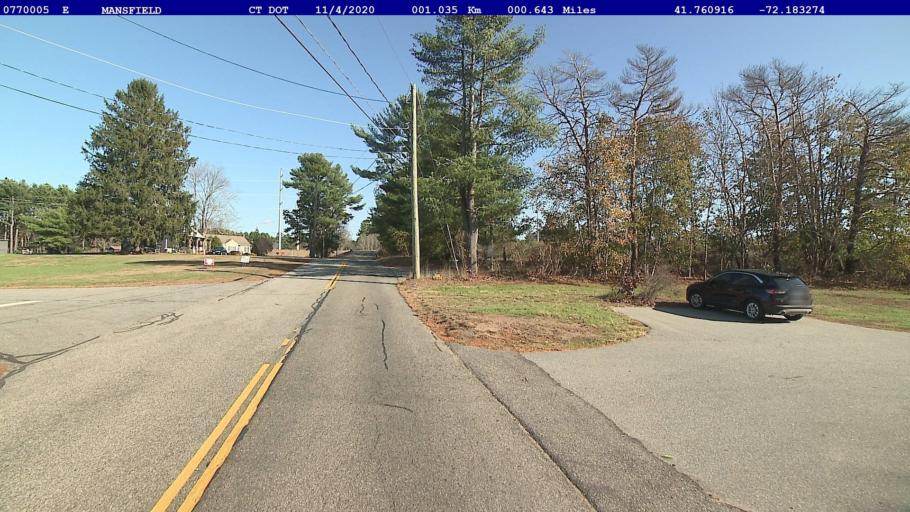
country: US
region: Connecticut
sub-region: Tolland County
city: Mansfield City
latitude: 41.7609
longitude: -72.1833
